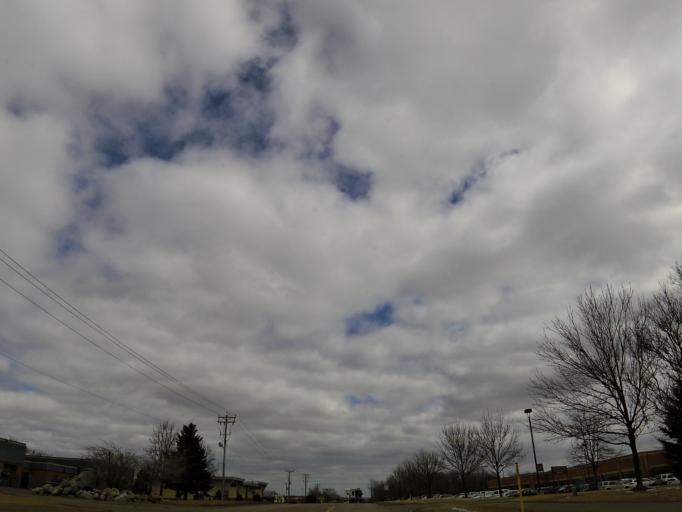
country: US
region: Minnesota
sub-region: Washington County
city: Oakdale
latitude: 44.9473
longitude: -92.9496
